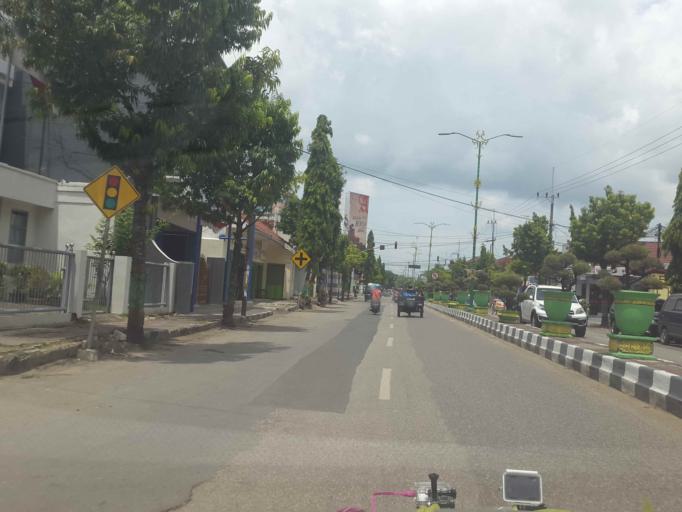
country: ID
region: East Java
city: Sumenep
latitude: -7.0136
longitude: 113.8585
